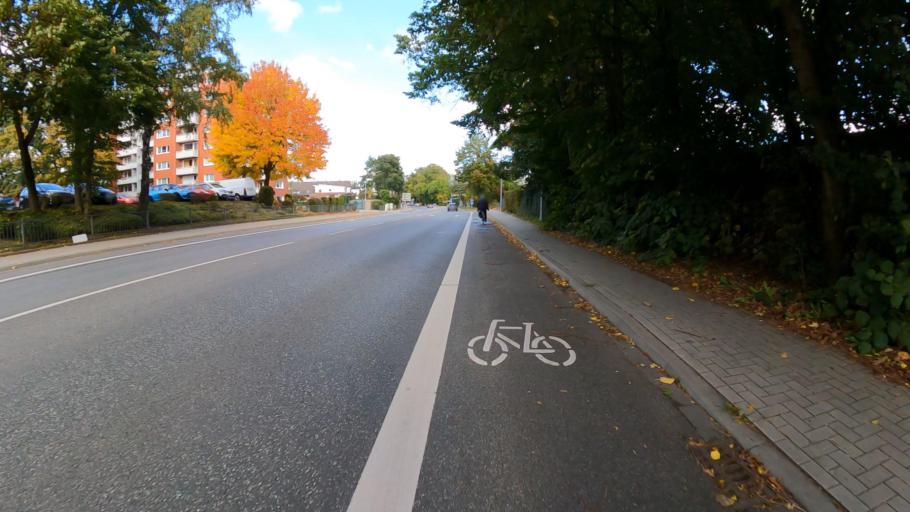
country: DE
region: Schleswig-Holstein
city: Norderstedt
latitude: 53.7067
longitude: 9.9977
